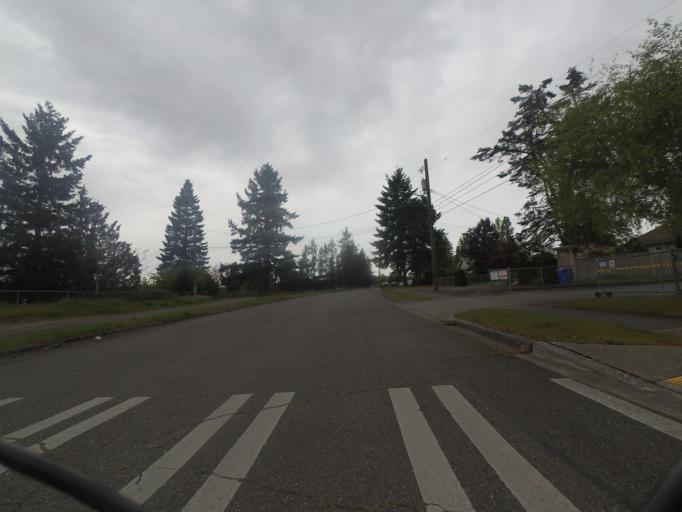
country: US
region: Washington
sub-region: Pierce County
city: Lakewood
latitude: 47.1975
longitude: -122.4761
